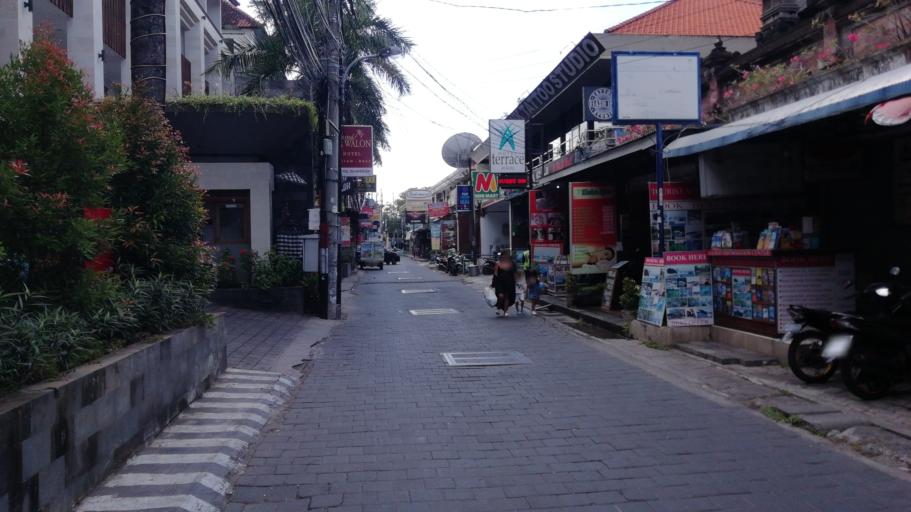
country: ID
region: Bali
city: Kuta
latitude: -8.7123
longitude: 115.1718
